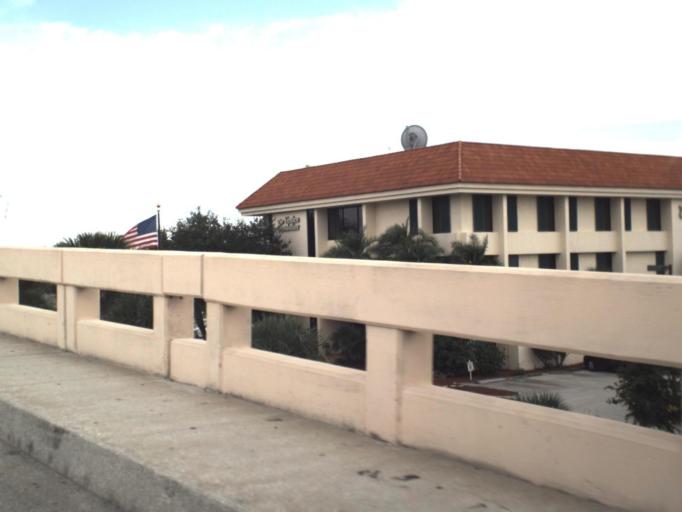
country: US
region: Florida
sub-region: Sarasota County
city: Venice
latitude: 27.0998
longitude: -82.4421
